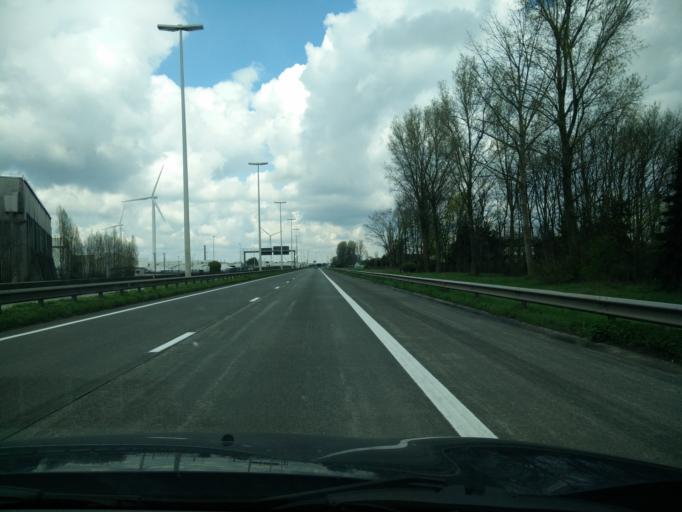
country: BE
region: Flanders
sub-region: Provincie Oost-Vlaanderen
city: Destelbergen
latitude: 51.0903
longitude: 3.7568
